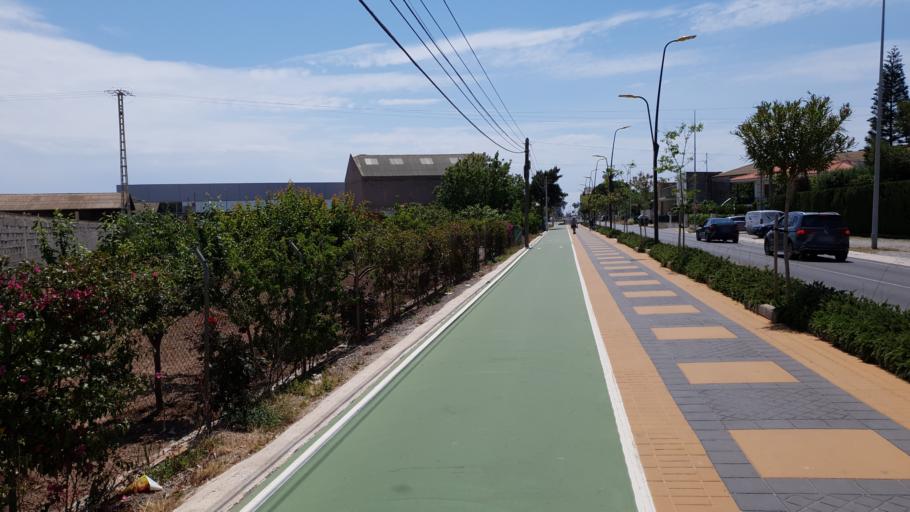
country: ES
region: Valencia
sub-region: Provincia de Castello
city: Burriana
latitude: 39.8727
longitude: -0.0753
